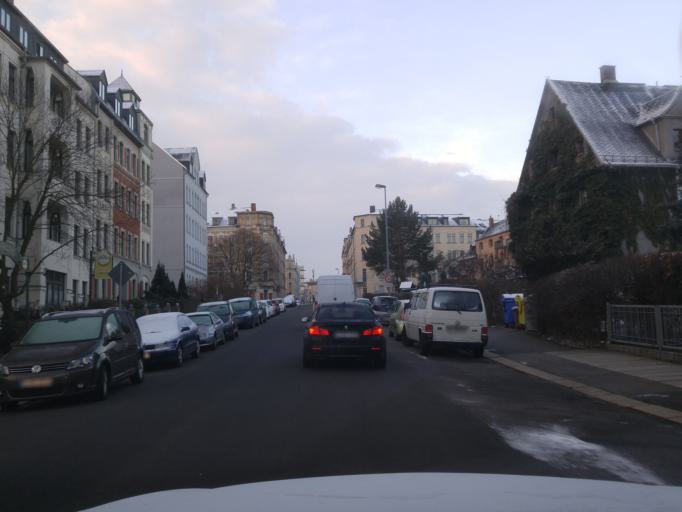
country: DE
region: Saxony
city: Chemnitz
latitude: 50.8461
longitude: 12.9085
